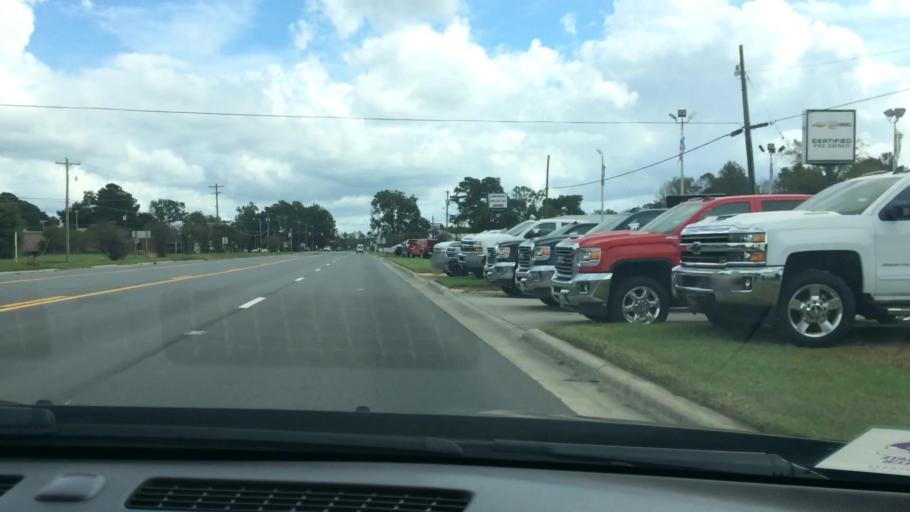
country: US
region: North Carolina
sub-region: Pitt County
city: Farmville
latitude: 35.5828
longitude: -77.5963
